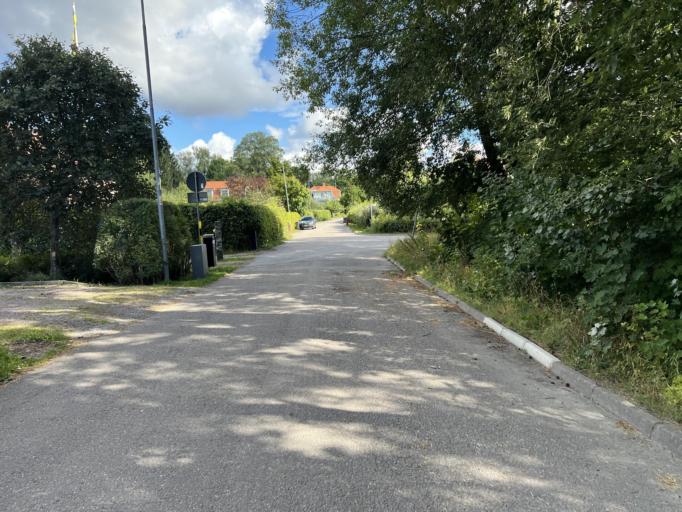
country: SE
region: Stockholm
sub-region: Vallentuna Kommun
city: Vallentuna
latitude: 59.5002
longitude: 18.0793
